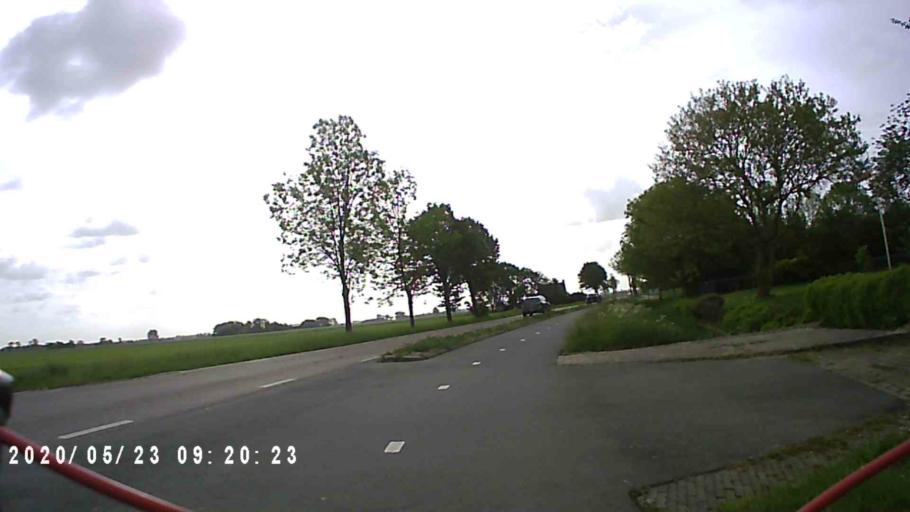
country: NL
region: Groningen
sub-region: Gemeente Bedum
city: Bedum
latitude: 53.2962
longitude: 6.6718
